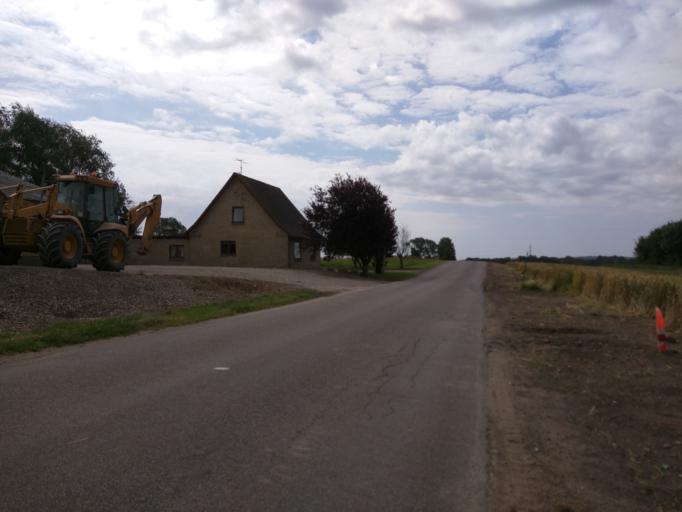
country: DK
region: Zealand
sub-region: Kalundborg Kommune
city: Svebolle
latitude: 55.6968
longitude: 11.3063
